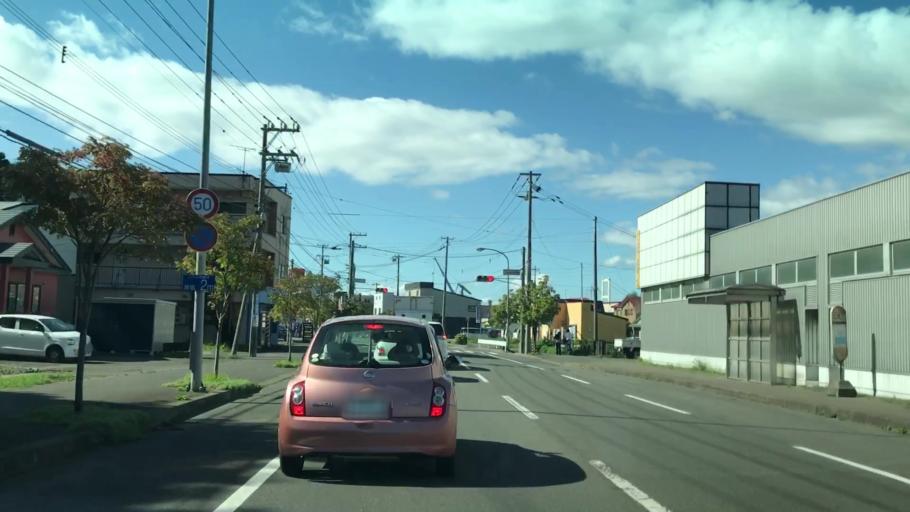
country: JP
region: Hokkaido
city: Muroran
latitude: 42.3331
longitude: 140.9626
